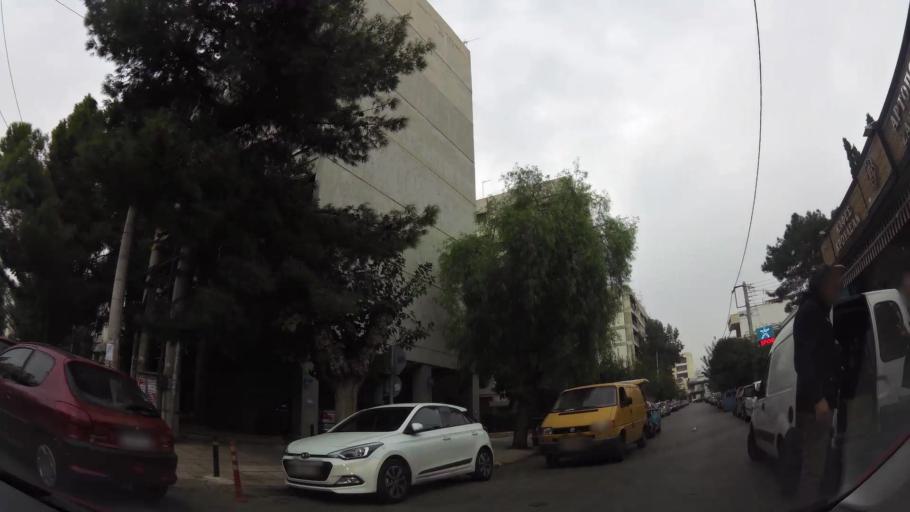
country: GR
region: Attica
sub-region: Nomarchia Athinas
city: Peristeri
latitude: 38.0073
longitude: 23.7003
